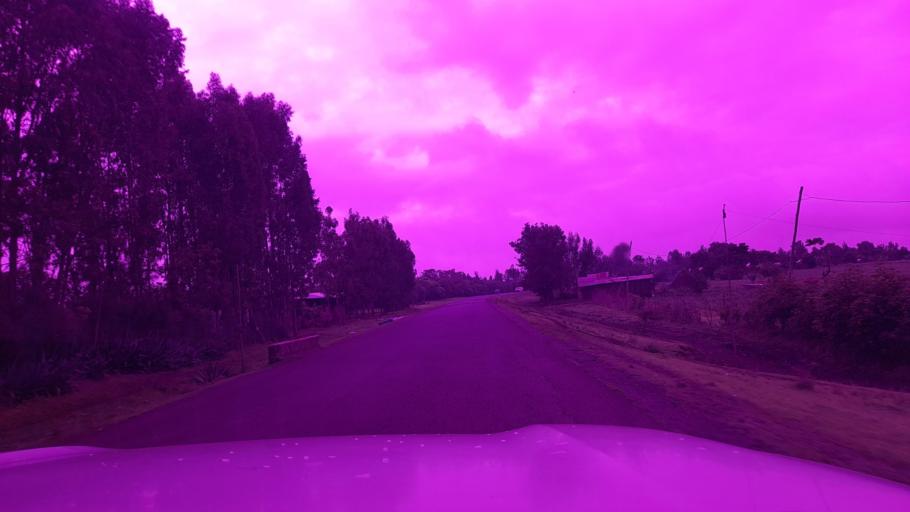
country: ET
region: Oromiya
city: Waliso
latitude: 8.2793
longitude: 37.6846
